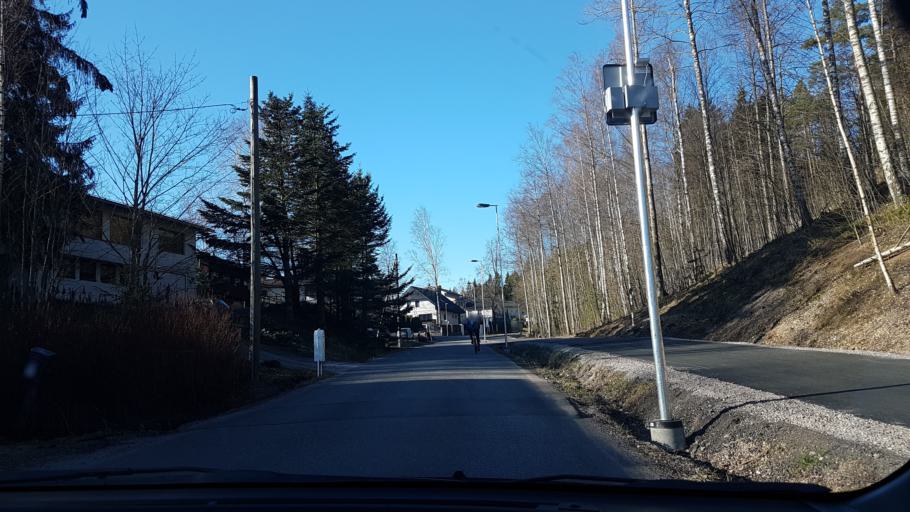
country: FI
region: Uusimaa
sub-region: Helsinki
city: Vantaa
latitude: 60.2705
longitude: 25.0906
